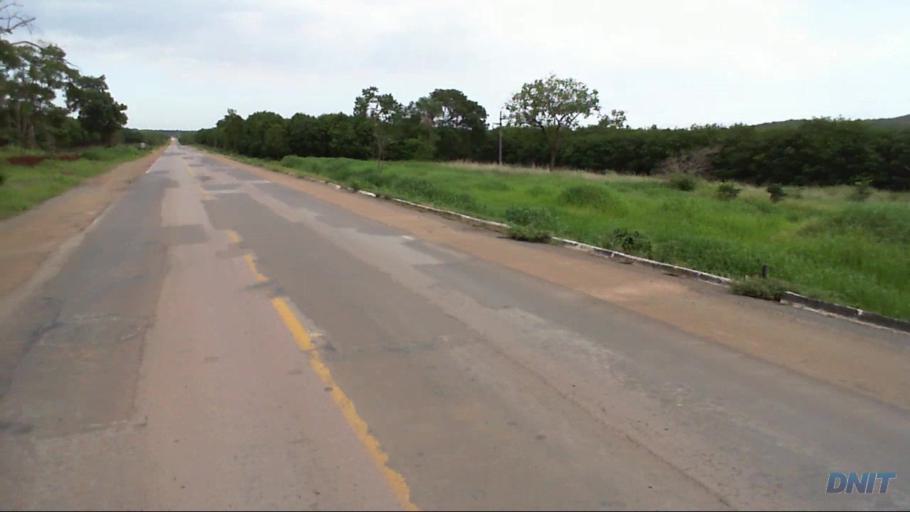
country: BR
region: Goias
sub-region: Barro Alto
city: Barro Alto
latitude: -14.8850
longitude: -48.9822
